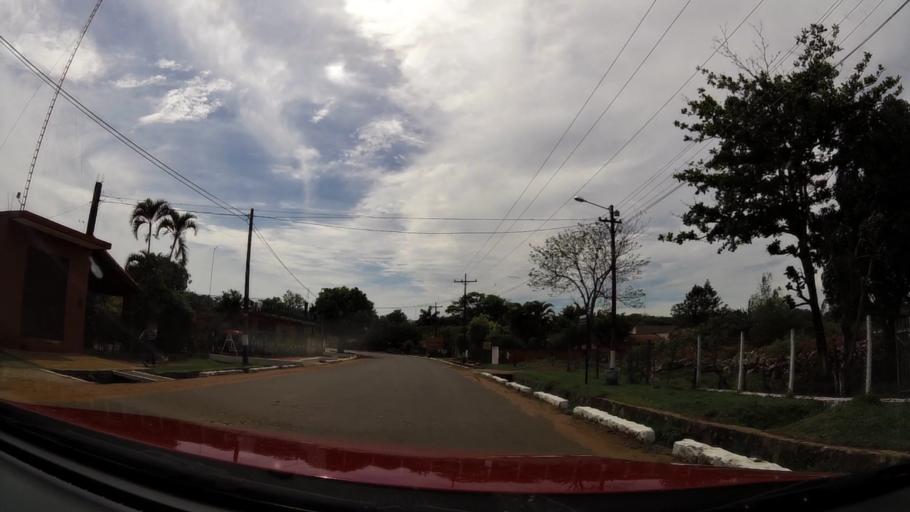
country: PY
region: Central
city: Limpio
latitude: -25.1811
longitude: -57.4454
